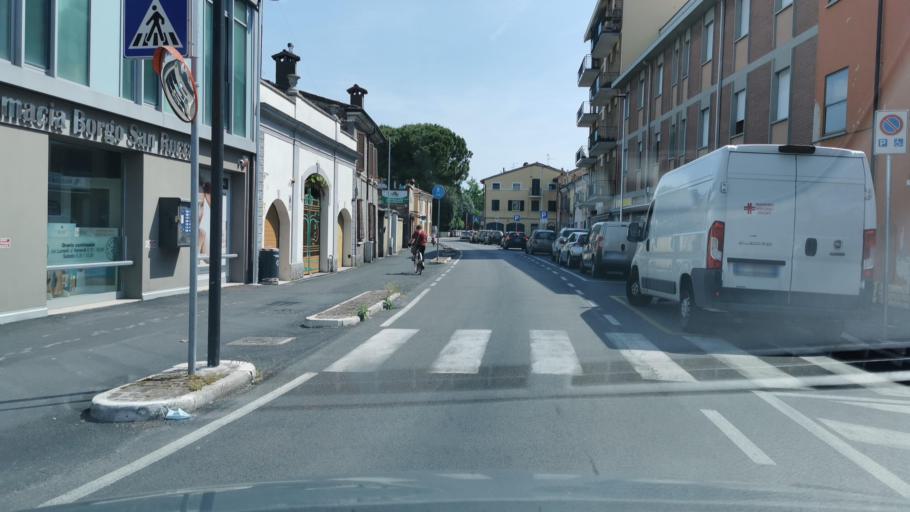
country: IT
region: Emilia-Romagna
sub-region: Provincia di Ravenna
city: Ravenna
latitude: 44.4112
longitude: 12.2006
